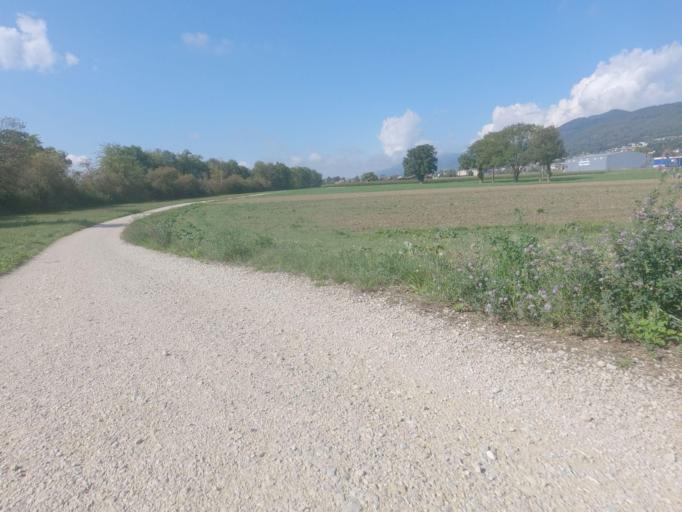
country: CH
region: Solothurn
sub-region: Bezirk Olten
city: Wangen
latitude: 47.3334
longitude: 7.8598
